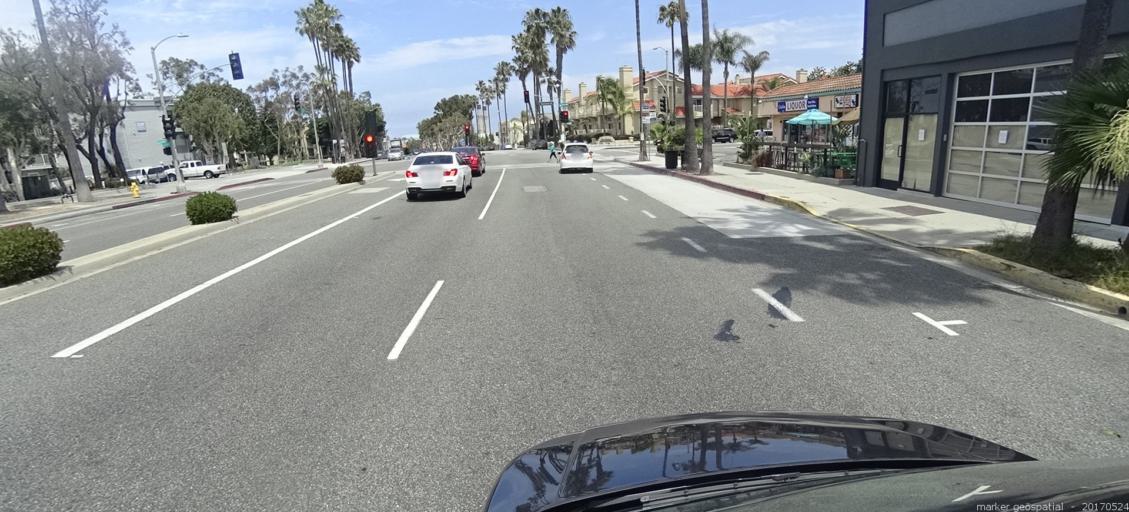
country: US
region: California
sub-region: Los Angeles County
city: Redondo Beach
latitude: 33.8430
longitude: -118.3889
